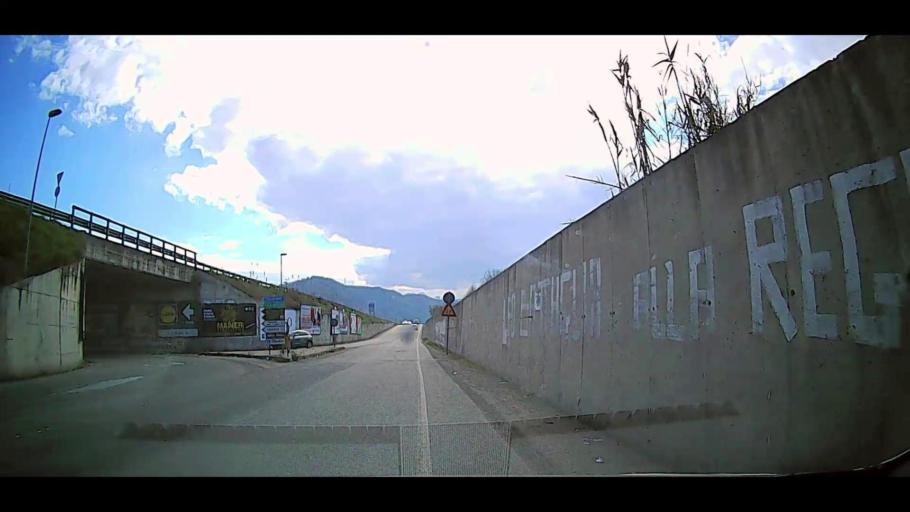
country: IT
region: Calabria
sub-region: Provincia di Cosenza
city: Cosenza
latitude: 39.3100
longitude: 16.2623
